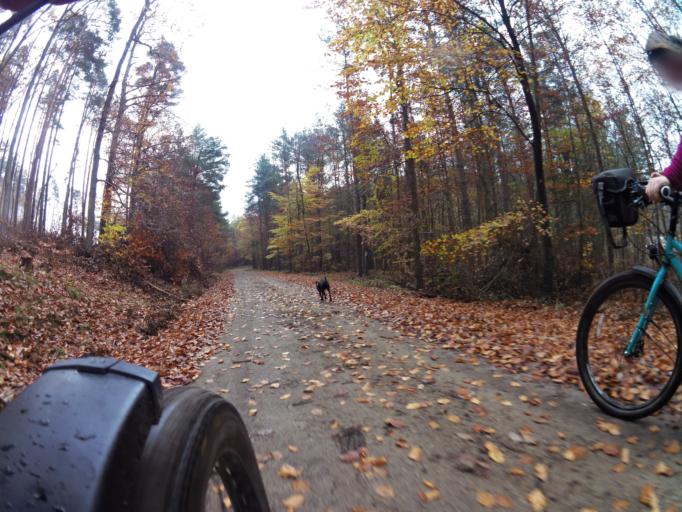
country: PL
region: Pomeranian Voivodeship
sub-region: Powiat pucki
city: Krokowa
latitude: 54.7469
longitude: 18.0935
